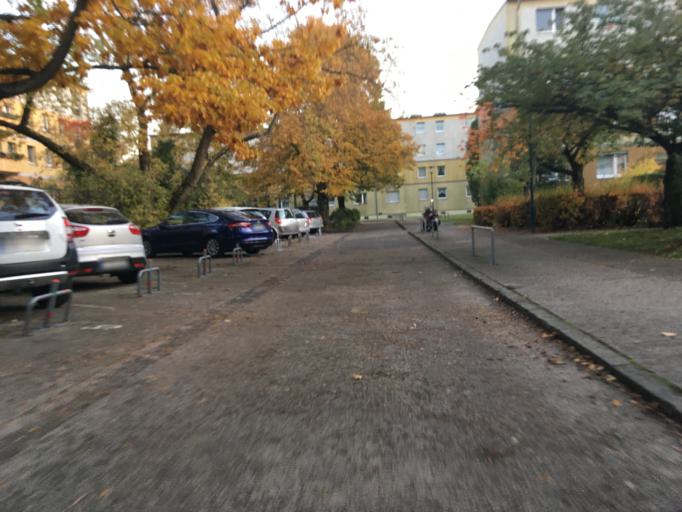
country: DE
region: Berlin
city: Heinersdorf
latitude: 52.5600
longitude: 13.4270
